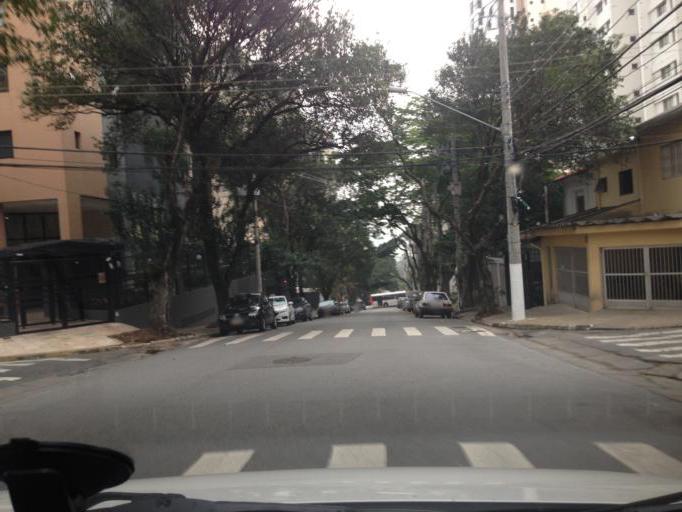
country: BR
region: Sao Paulo
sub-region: Osasco
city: Osasco
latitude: -23.5331
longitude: -46.7168
